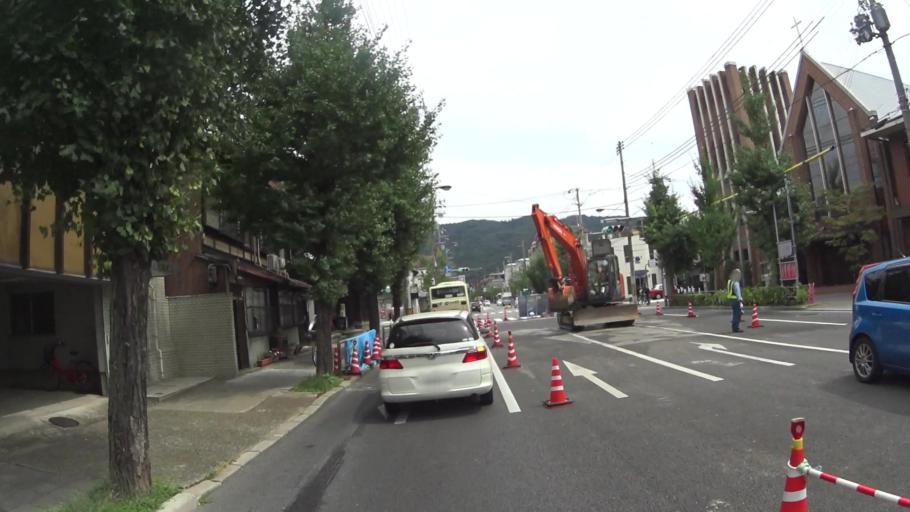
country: JP
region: Kyoto
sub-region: Kyoto-shi
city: Kamigyo-ku
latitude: 35.0174
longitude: 135.7841
